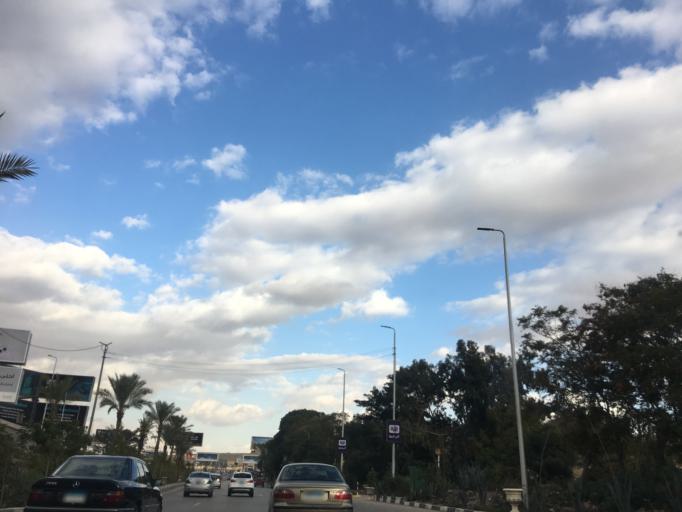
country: EG
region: Muhafazat al Qahirah
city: Cairo
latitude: 30.0229
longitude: 31.3538
